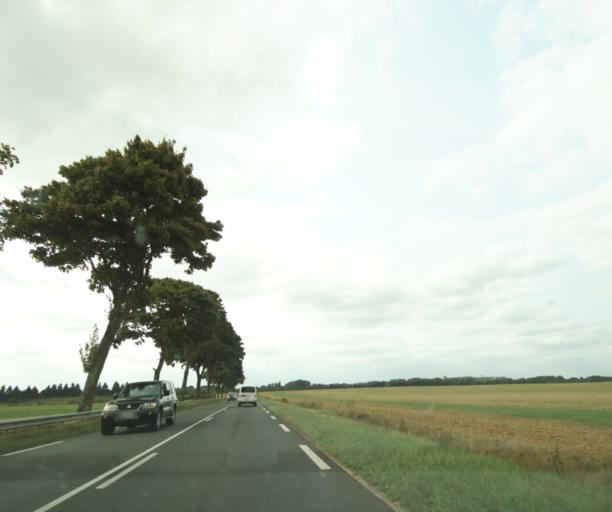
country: FR
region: Centre
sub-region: Departement d'Indre-et-Loire
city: Reignac-sur-Indre
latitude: 47.2033
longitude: 0.9098
